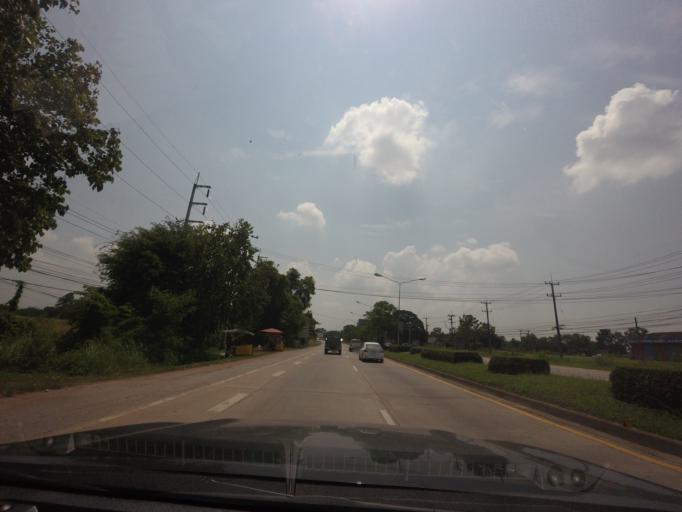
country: TH
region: Uttaradit
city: Uttaradit
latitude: 17.6070
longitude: 100.1232
